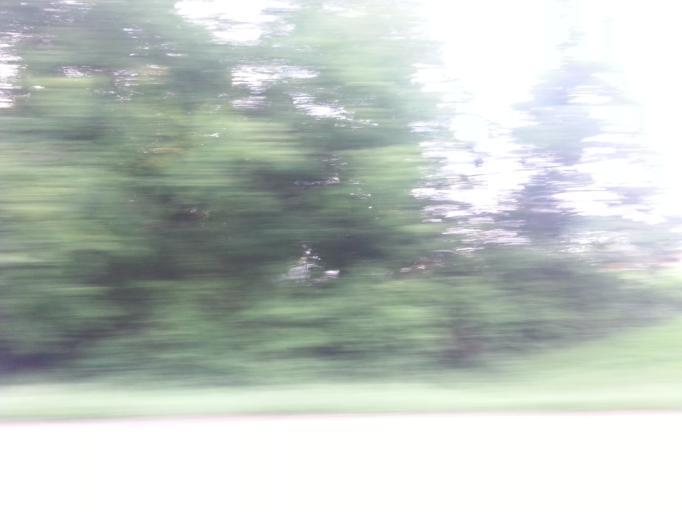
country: US
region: Tennessee
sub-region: Anderson County
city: Norris
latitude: 36.1049
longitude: -83.9660
